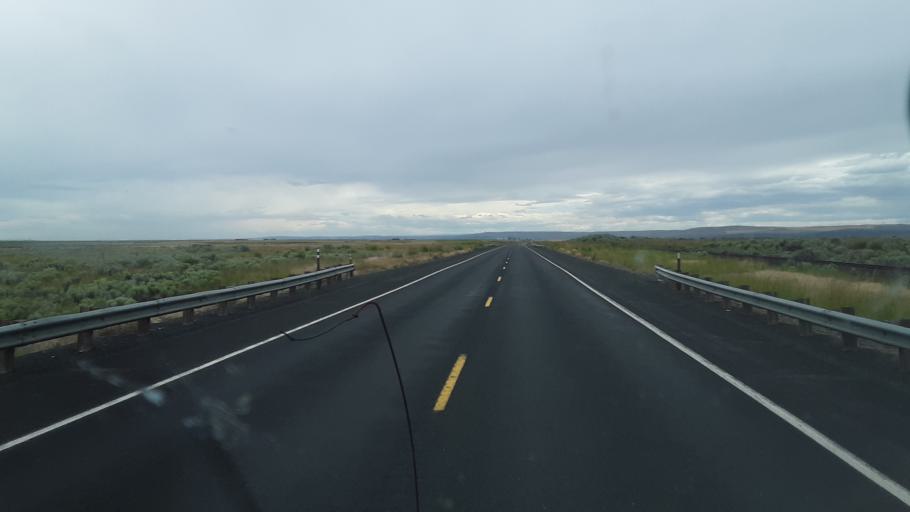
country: US
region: Washington
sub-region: Okanogan County
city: Coulee Dam
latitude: 47.6687
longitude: -119.1819
